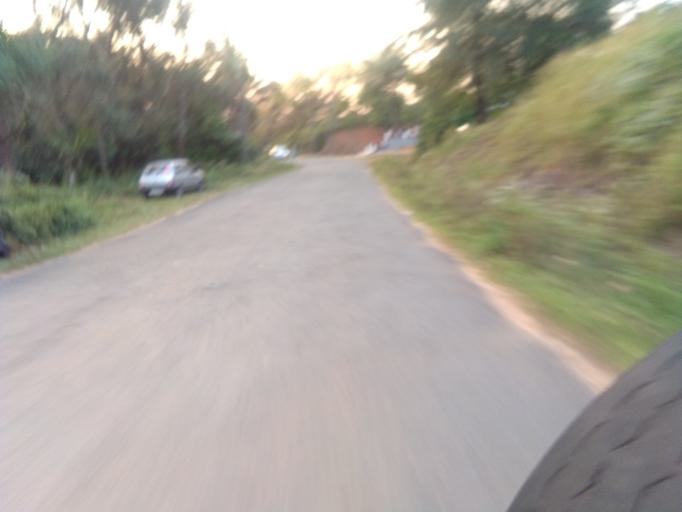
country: IN
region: Kerala
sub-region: Idukki
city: Idukki
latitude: 9.9732
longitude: 76.8640
